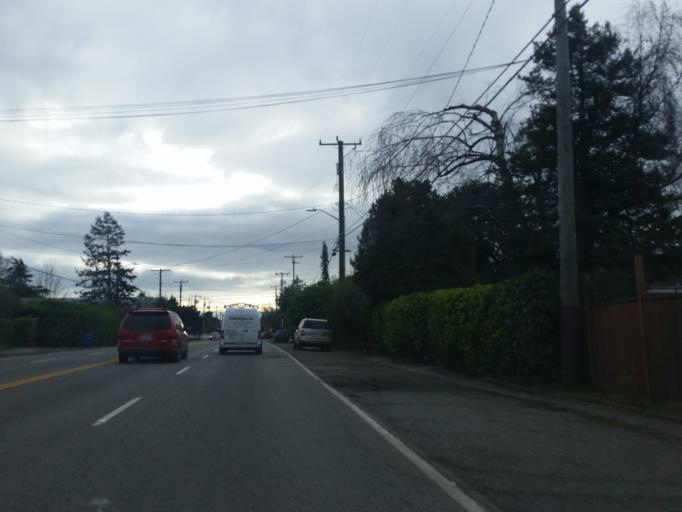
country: US
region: Washington
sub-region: King County
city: Shoreline
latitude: 47.7170
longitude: -122.3556
